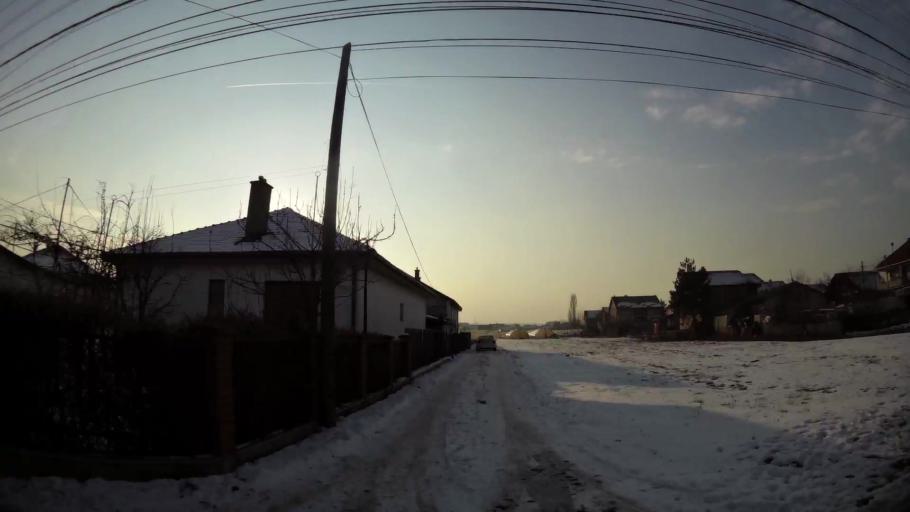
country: MK
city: Creshevo
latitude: 42.0237
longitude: 21.5202
